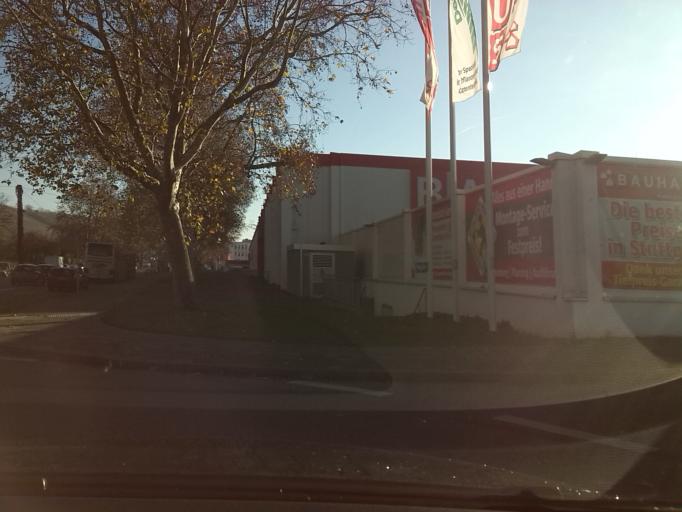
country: DE
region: Baden-Wuerttemberg
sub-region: Regierungsbezirk Stuttgart
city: Fellbach
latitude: 48.7751
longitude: 9.2591
